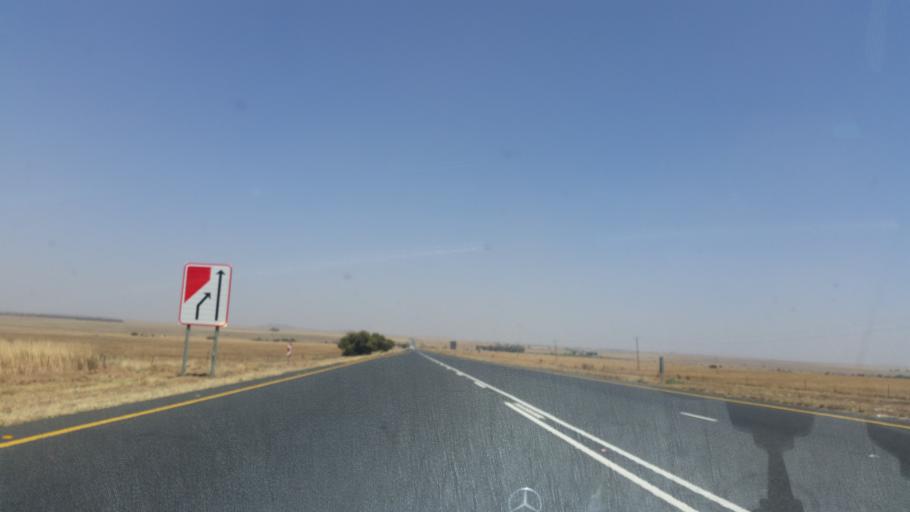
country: ZA
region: Orange Free State
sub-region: Lejweleputswa District Municipality
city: Winburg
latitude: -28.7170
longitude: 26.7751
